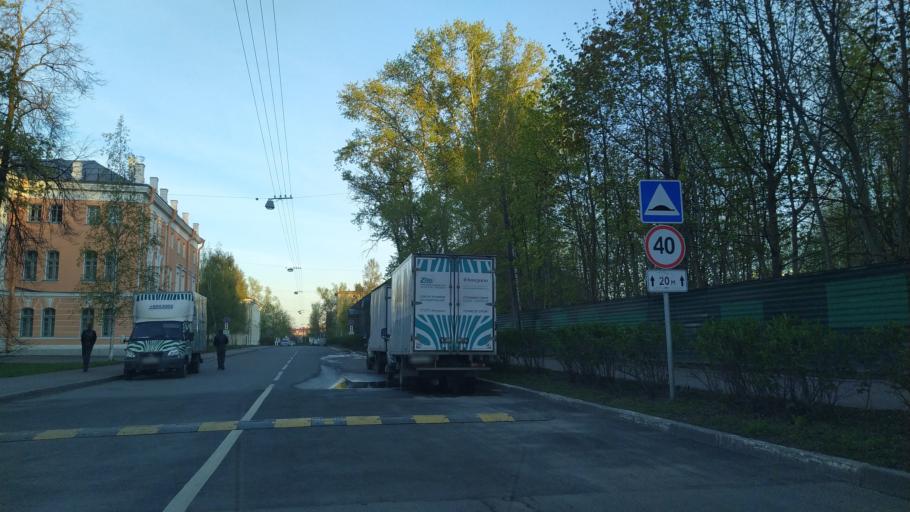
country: RU
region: St.-Petersburg
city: Pushkin
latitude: 59.7066
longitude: 30.4098
